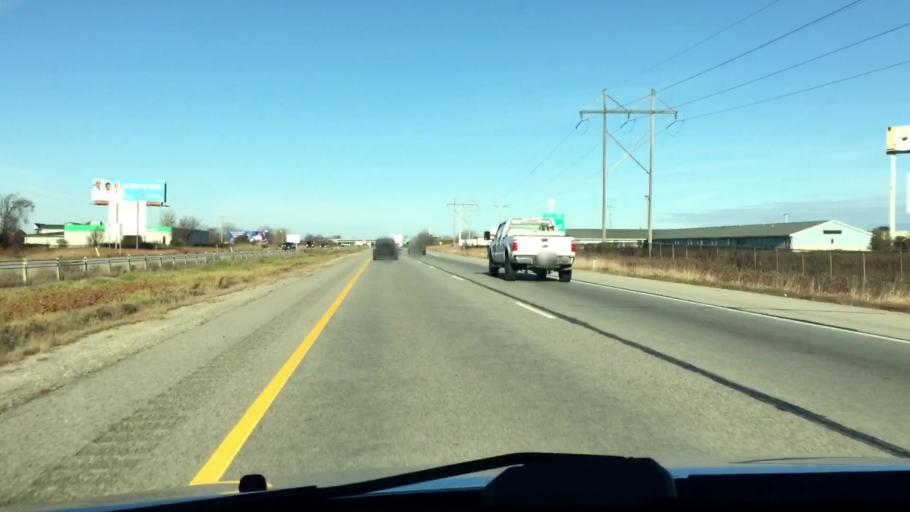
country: US
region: Wisconsin
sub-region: Fond du Lac County
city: North Fond du Lac
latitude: 43.8022
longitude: -88.4926
